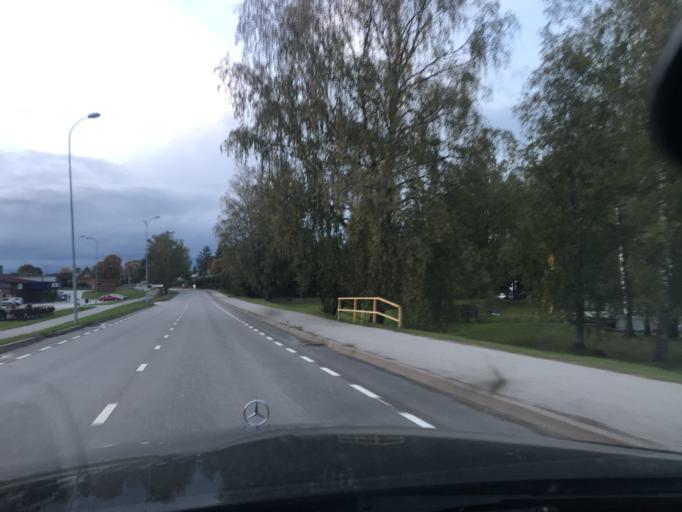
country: EE
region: Valgamaa
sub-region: Torva linn
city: Torva
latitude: 57.9970
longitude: 25.9347
